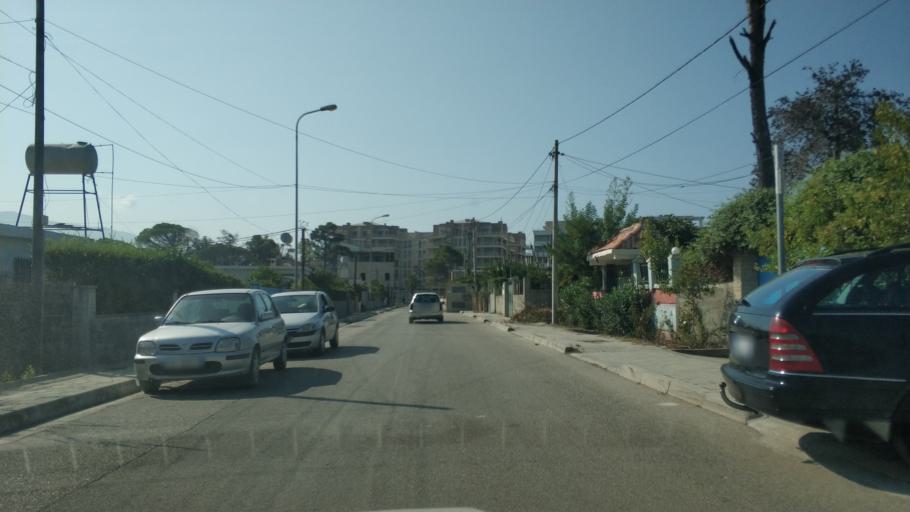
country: AL
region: Vlore
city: Vlore
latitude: 40.4598
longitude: 19.4690
